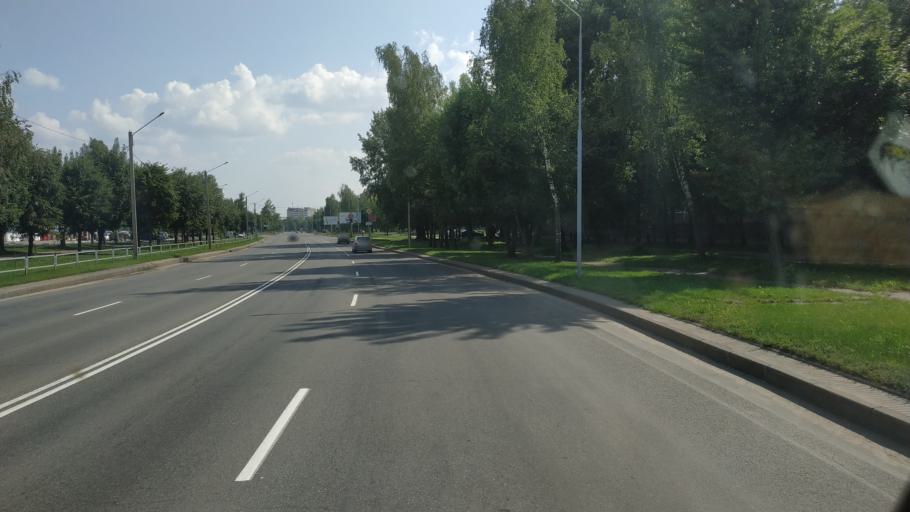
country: BY
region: Mogilev
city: Buynichy
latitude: 53.8746
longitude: 30.3123
